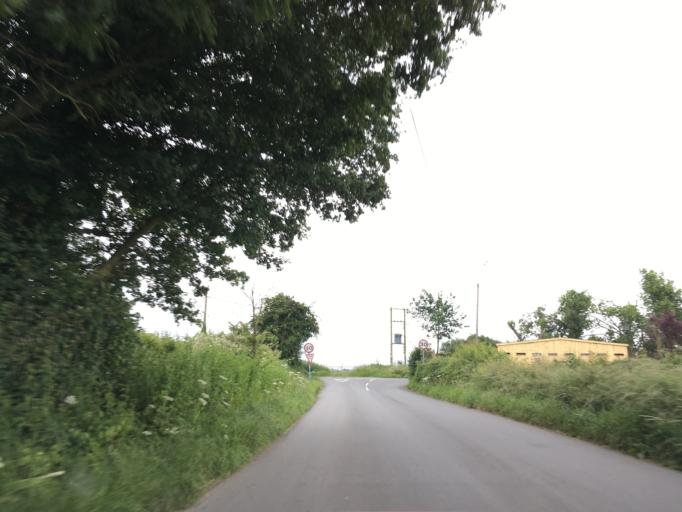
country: GB
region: England
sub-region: Gloucestershire
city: Stonehouse
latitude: 51.7780
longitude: -2.3558
